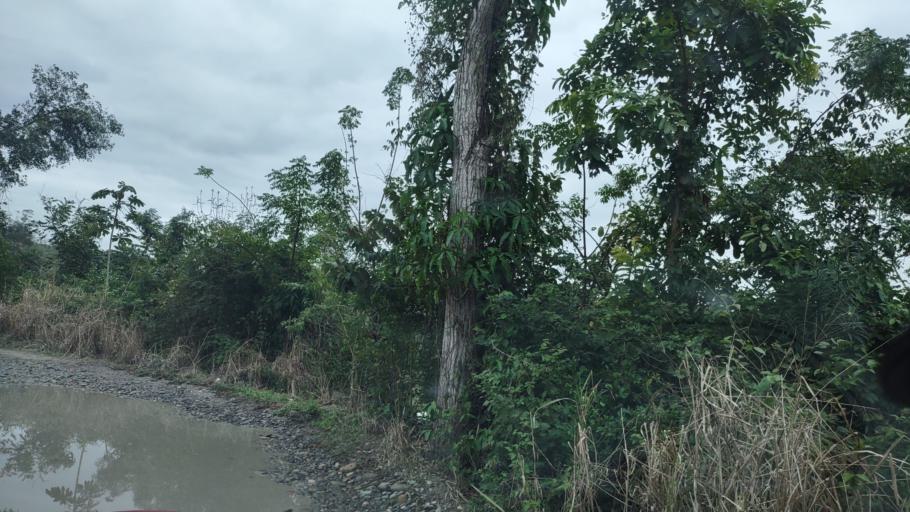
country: MX
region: Veracruz
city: Papantla de Olarte
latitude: 20.4241
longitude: -97.2711
